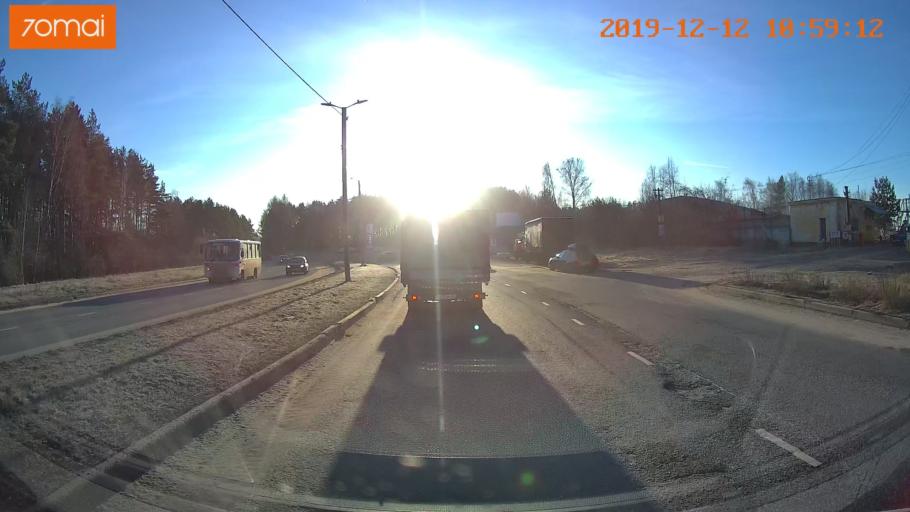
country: RU
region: Ivanovo
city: Kokhma
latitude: 56.9664
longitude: 41.0591
